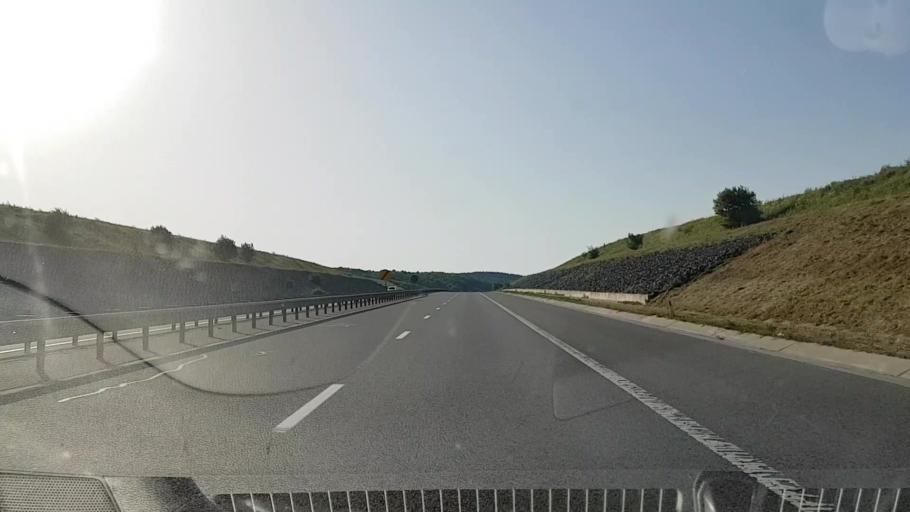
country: RO
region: Cluj
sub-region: Comuna Savadisla
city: Savadisla
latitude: 46.6597
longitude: 23.4976
